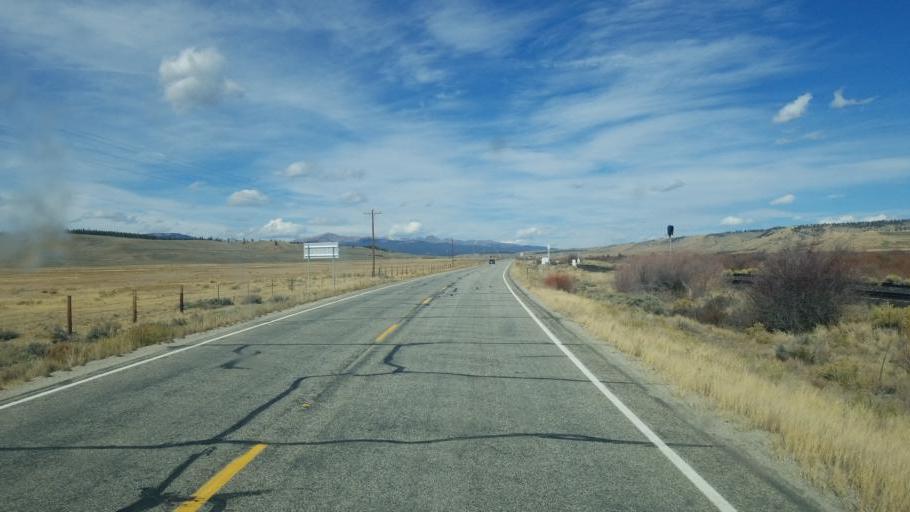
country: US
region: Colorado
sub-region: Lake County
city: Leadville
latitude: 39.1328
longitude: -106.3168
